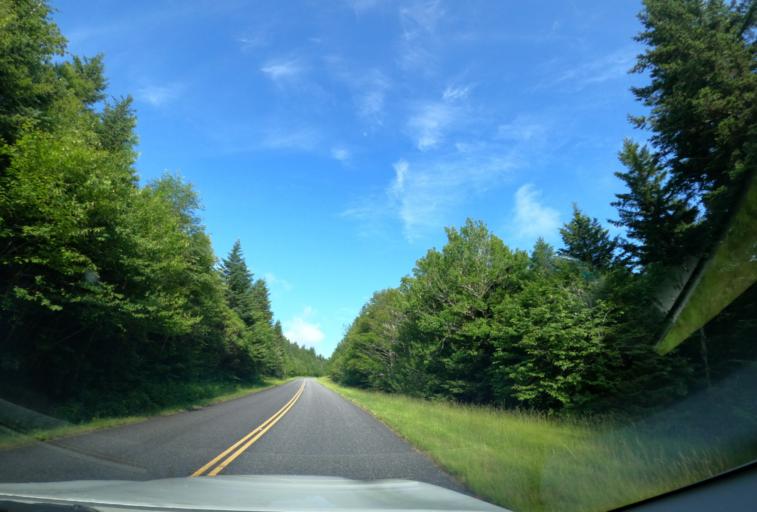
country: US
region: North Carolina
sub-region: Haywood County
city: Hazelwood
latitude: 35.2994
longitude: -82.9226
